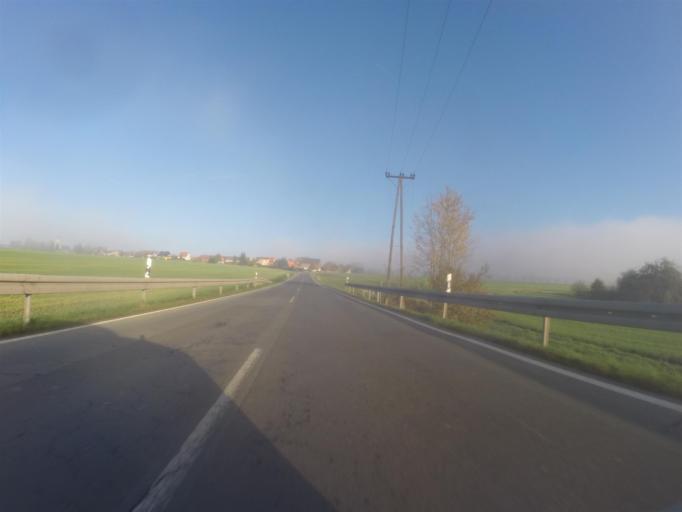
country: DE
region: Thuringia
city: Walpernhain
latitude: 51.0168
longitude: 11.9194
